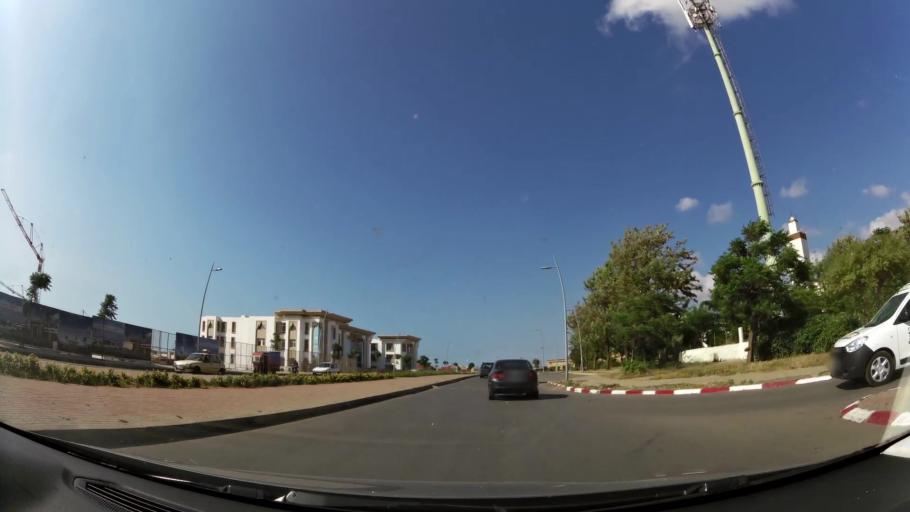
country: MA
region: Rabat-Sale-Zemmour-Zaer
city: Sale
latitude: 34.0463
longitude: -6.7889
